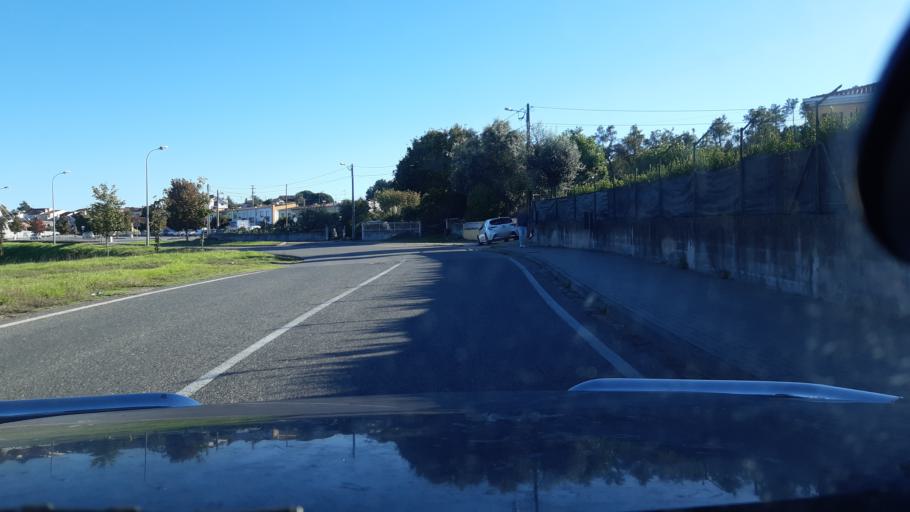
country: PT
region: Aveiro
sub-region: Agueda
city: Agueda
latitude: 40.5643
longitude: -8.4444
